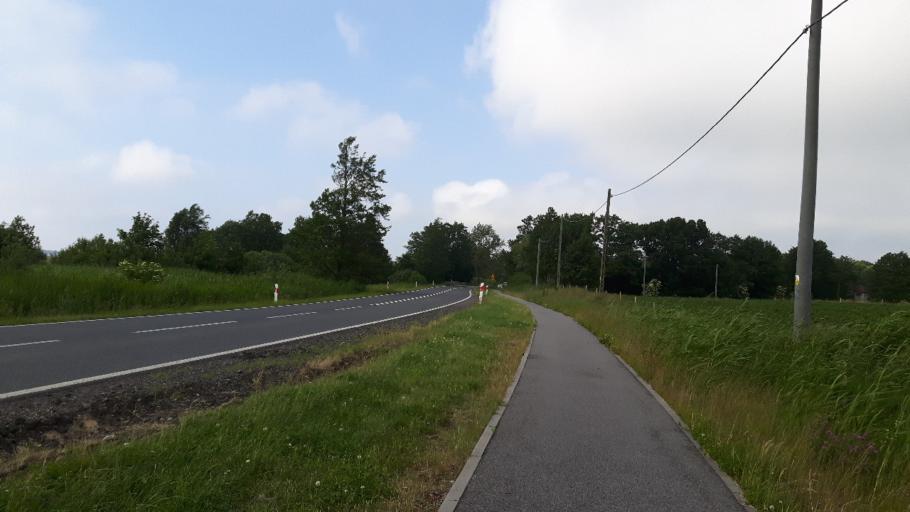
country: PL
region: West Pomeranian Voivodeship
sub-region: Powiat slawienski
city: Darlowo
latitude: 54.3488
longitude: 16.3326
